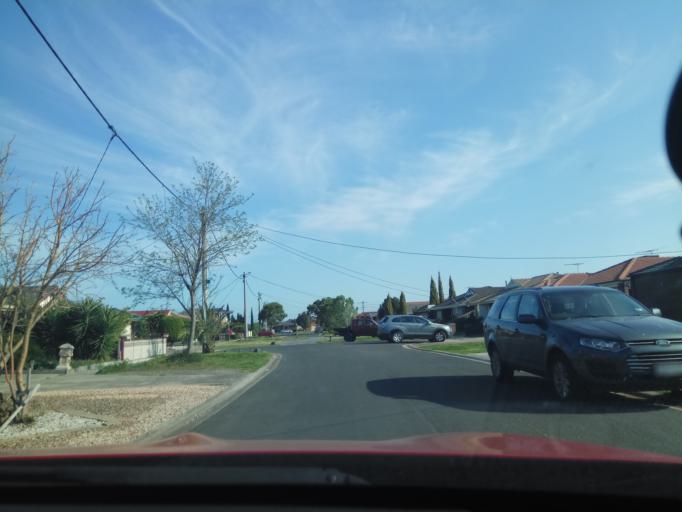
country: AU
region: Victoria
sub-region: Hobsons Bay
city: Altona Meadows
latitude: -37.8775
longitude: 144.7711
